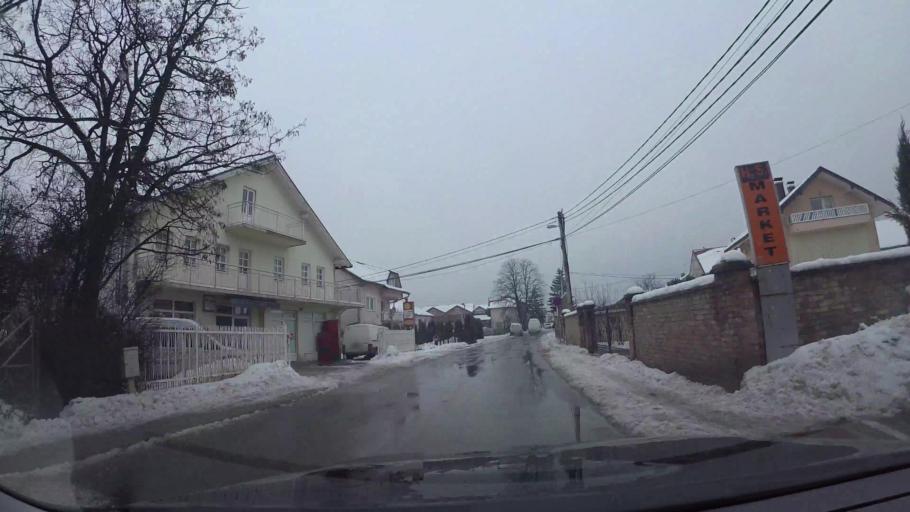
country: BA
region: Federation of Bosnia and Herzegovina
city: Hadzici
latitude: 43.8407
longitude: 18.2771
